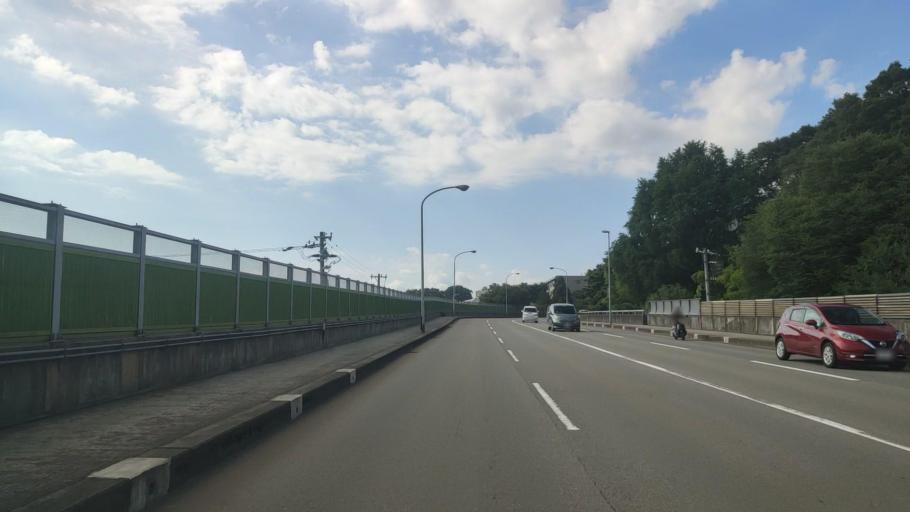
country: JP
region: Ishikawa
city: Nonoichi
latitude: 36.5483
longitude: 136.6600
